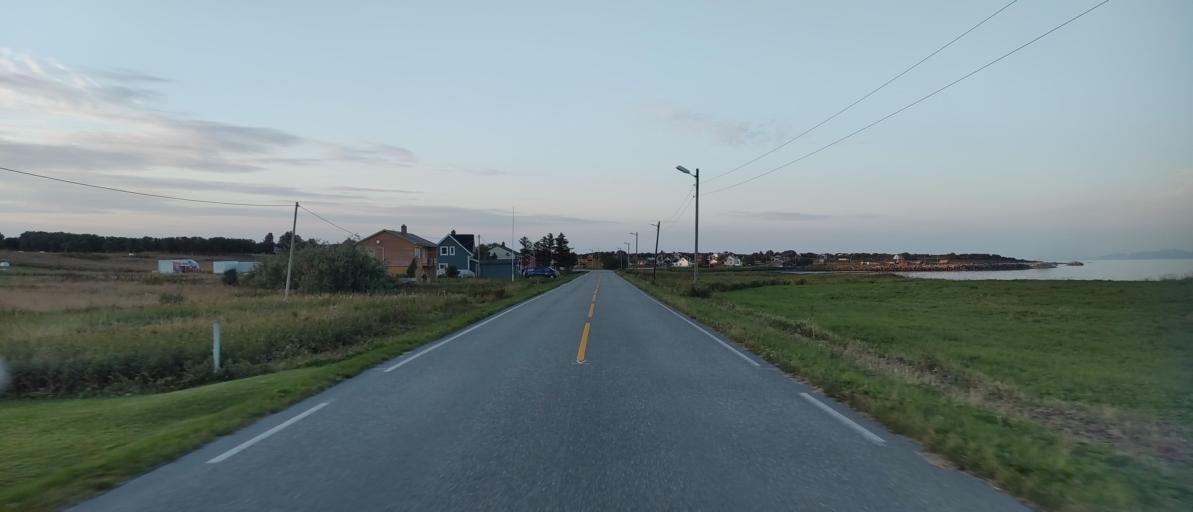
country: NO
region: Nordland
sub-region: Andoy
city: Andenes
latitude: 69.2418
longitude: 16.1155
